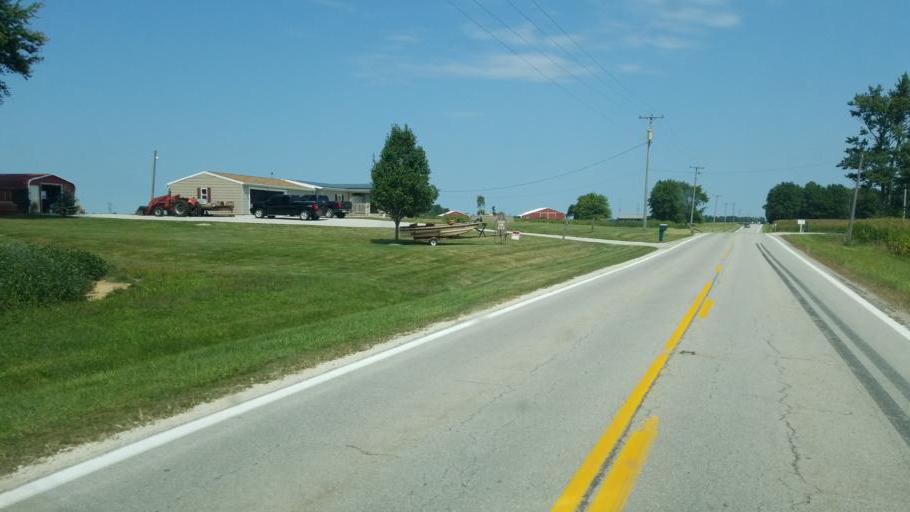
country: US
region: Ohio
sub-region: Marion County
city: Marion
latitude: 40.6974
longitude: -83.1464
